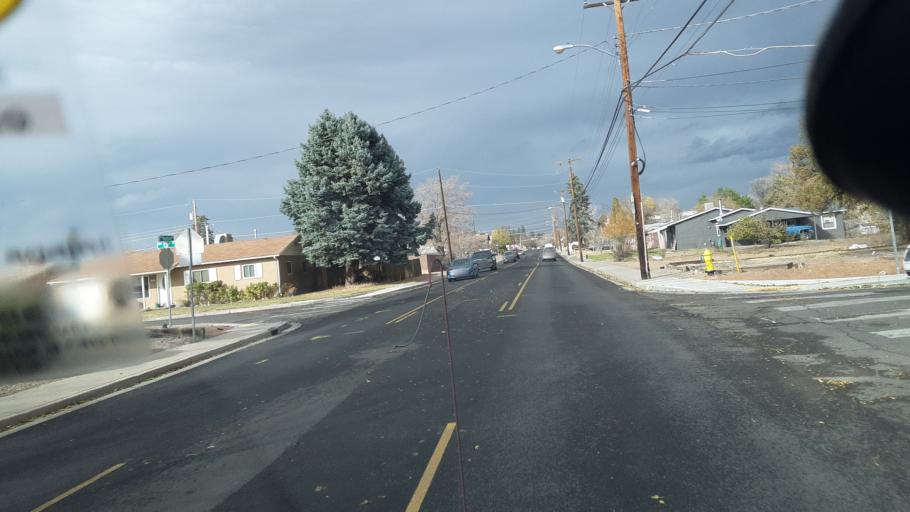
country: US
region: New Mexico
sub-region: San Juan County
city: Farmington
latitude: 36.7446
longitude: -108.1978
